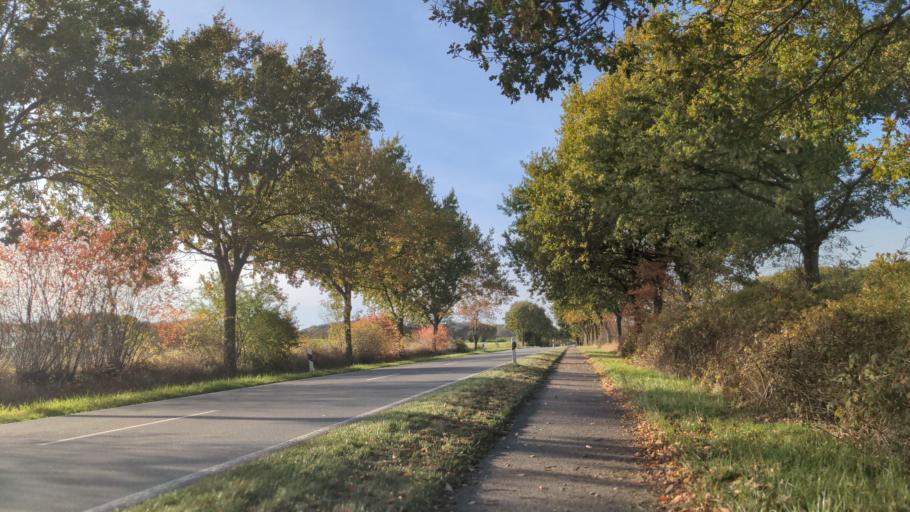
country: DE
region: Schleswig-Holstein
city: Kirchnuchel
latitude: 54.1995
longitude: 10.6946
